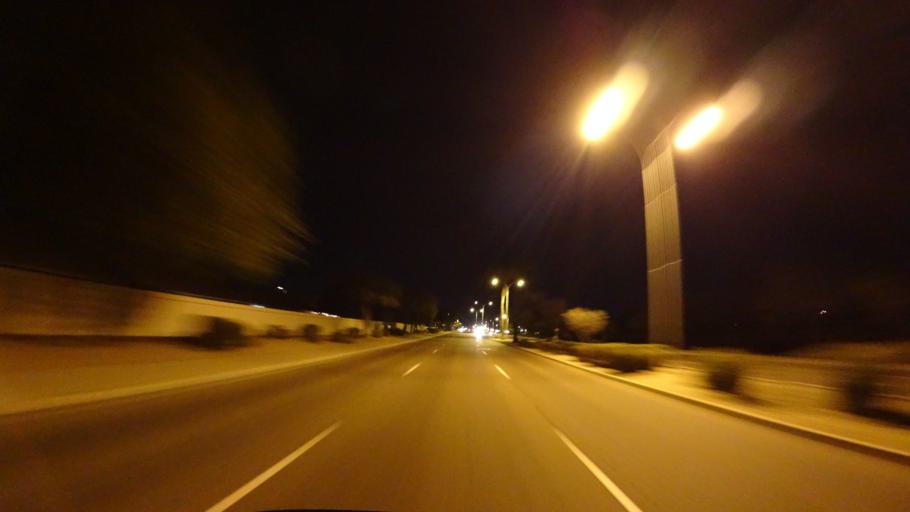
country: US
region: Arizona
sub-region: Maricopa County
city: Chandler
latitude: 33.3206
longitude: -111.8655
